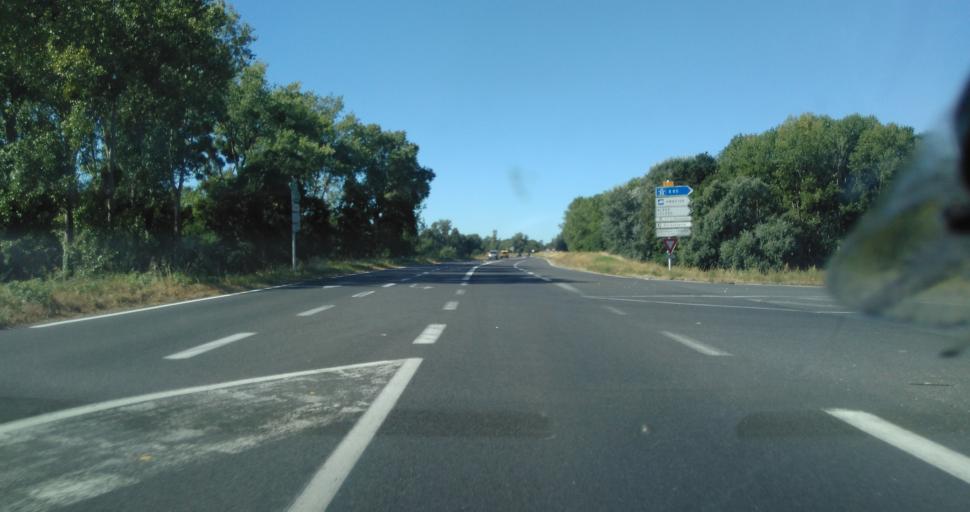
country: FR
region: Centre
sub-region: Departement d'Indre-et-Loire
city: Poce-sur-Cisse
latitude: 47.4303
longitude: 1.0067
